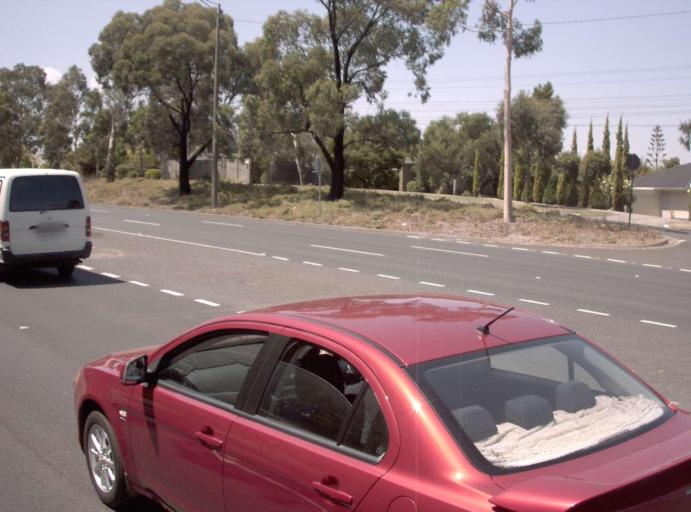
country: AU
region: Victoria
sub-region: Whitehorse
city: Vermont South
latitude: -37.8651
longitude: 145.1685
